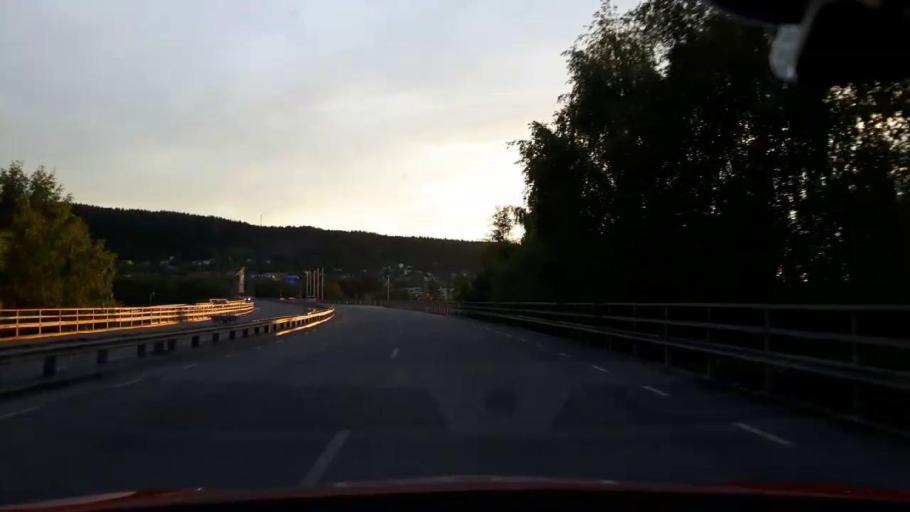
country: SE
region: Jaemtland
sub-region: OEstersunds Kommun
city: Ostersund
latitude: 63.1811
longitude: 14.6319
